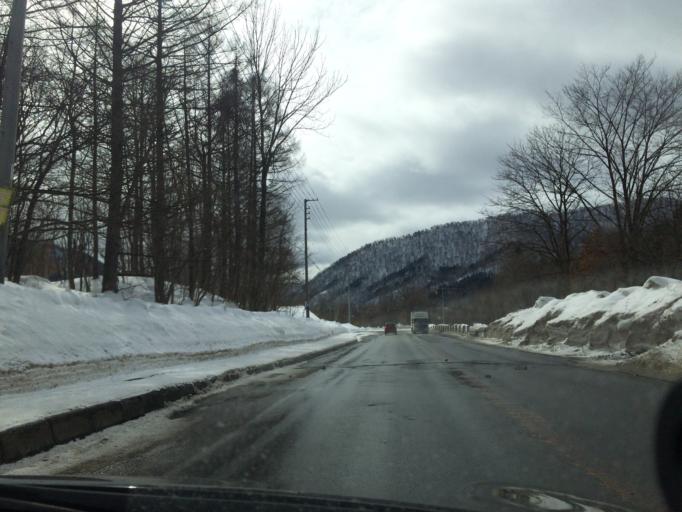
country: JP
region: Hokkaido
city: Iwamizawa
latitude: 42.9477
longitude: 142.0401
